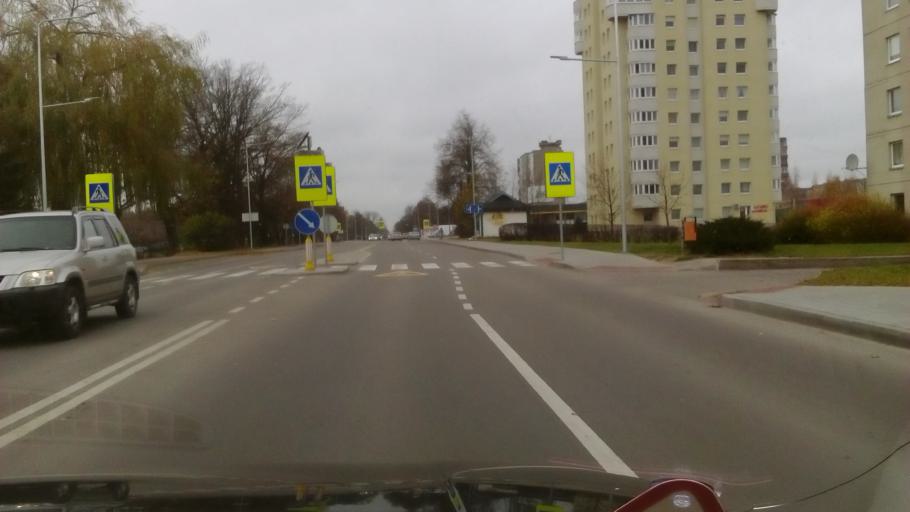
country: LT
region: Marijampoles apskritis
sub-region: Marijampole Municipality
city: Marijampole
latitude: 54.5621
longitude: 23.3354
